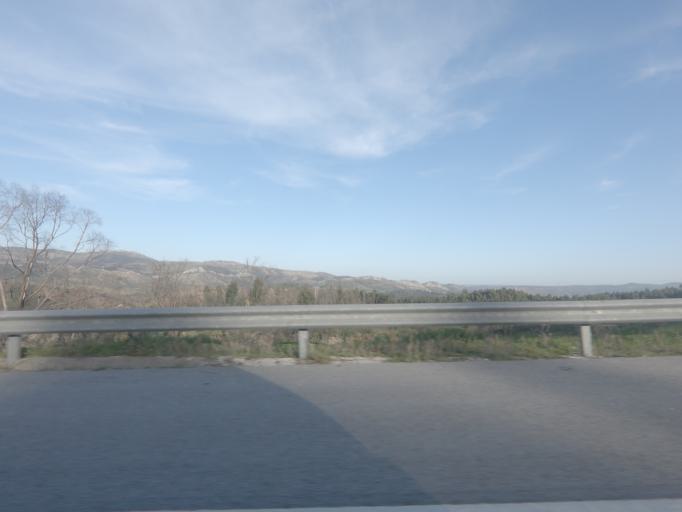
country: PT
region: Portalegre
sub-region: Nisa
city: Nisa
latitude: 39.6586
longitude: -7.7380
